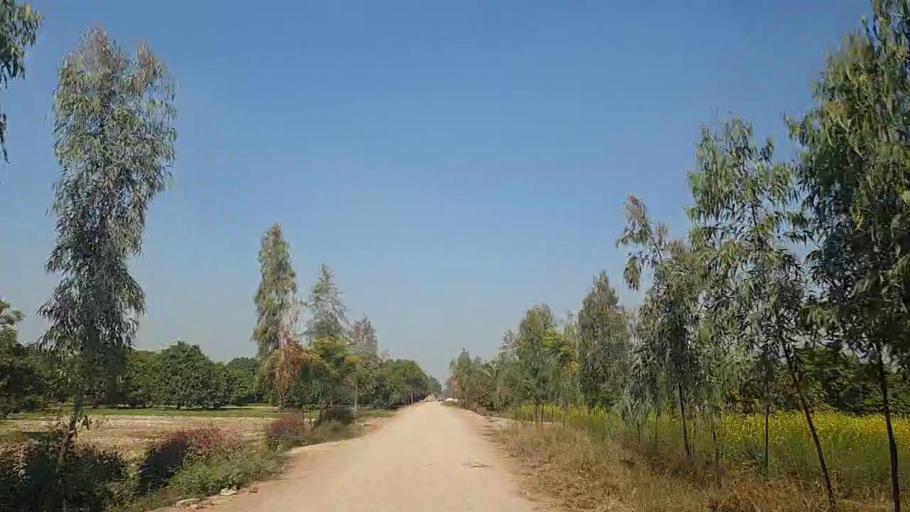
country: PK
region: Sindh
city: Nawabshah
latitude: 26.2414
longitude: 68.3383
